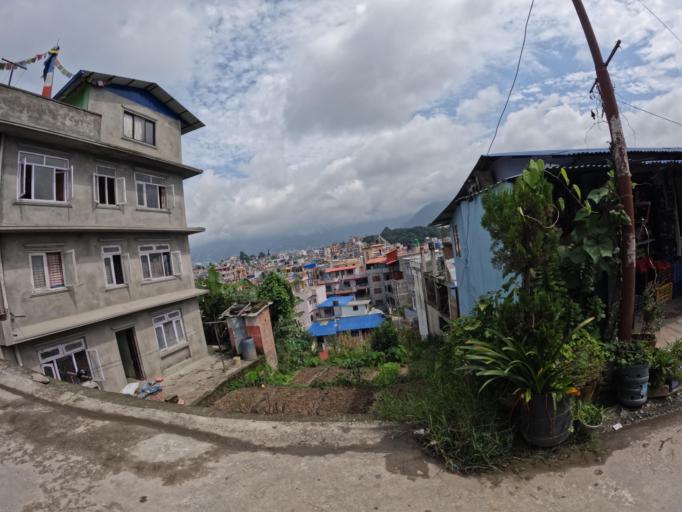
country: NP
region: Central Region
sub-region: Bagmati Zone
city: Kathmandu
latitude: 27.7544
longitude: 85.3225
